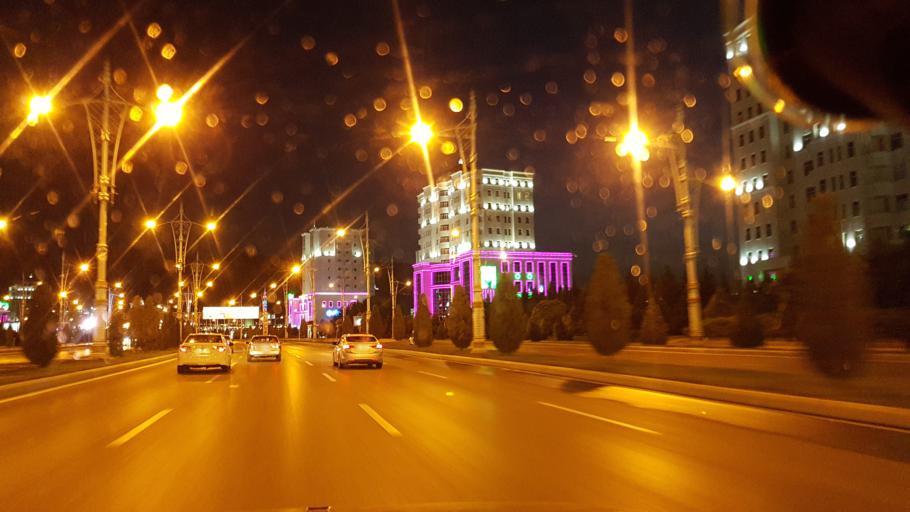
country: TM
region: Ahal
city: Ashgabat
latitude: 37.9165
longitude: 58.3465
